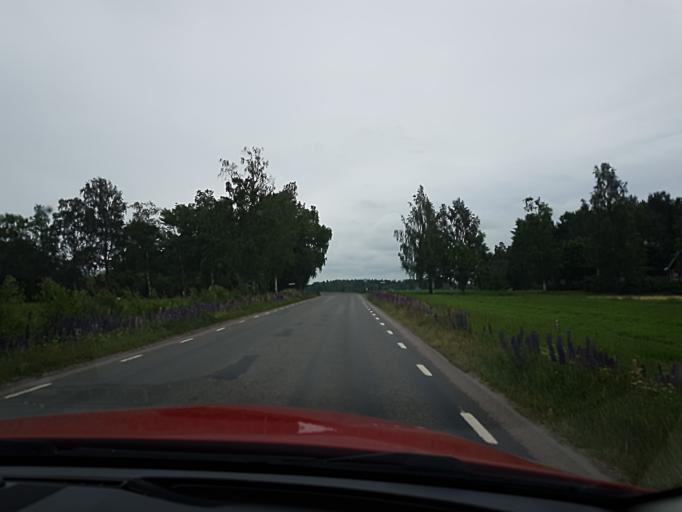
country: SE
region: Vaestra Goetaland
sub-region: Skovde Kommun
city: Skoevde
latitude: 58.3816
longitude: 13.9212
